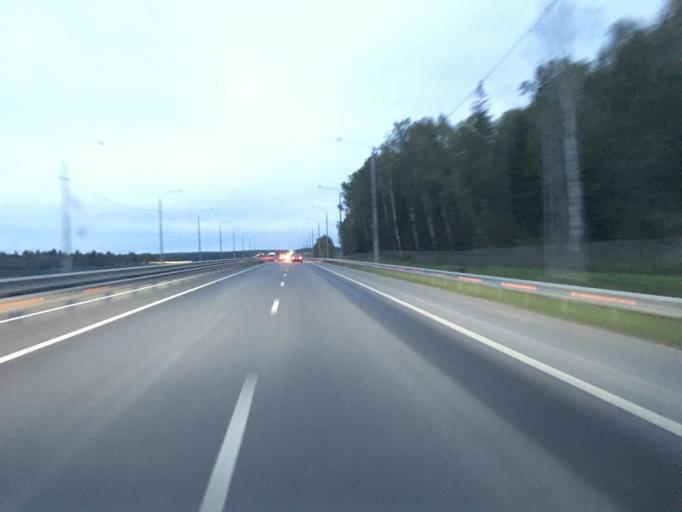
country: RU
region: Kaluga
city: Maloyaroslavets
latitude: 54.9442
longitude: 36.4360
